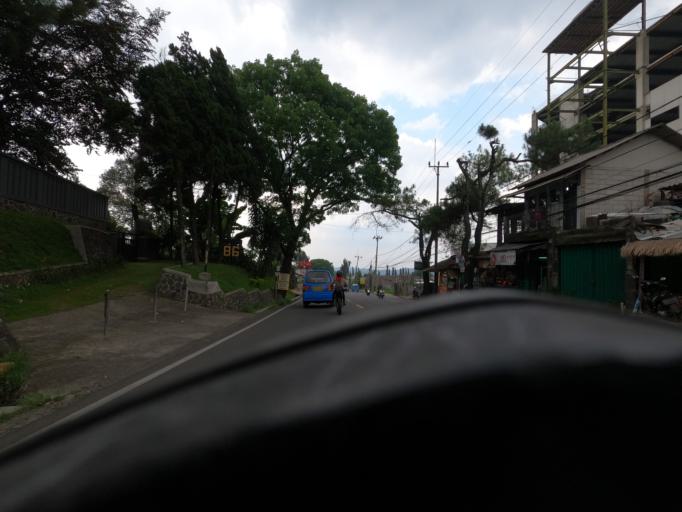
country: ID
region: West Java
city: Caringin
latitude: -6.6628
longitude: 106.9191
